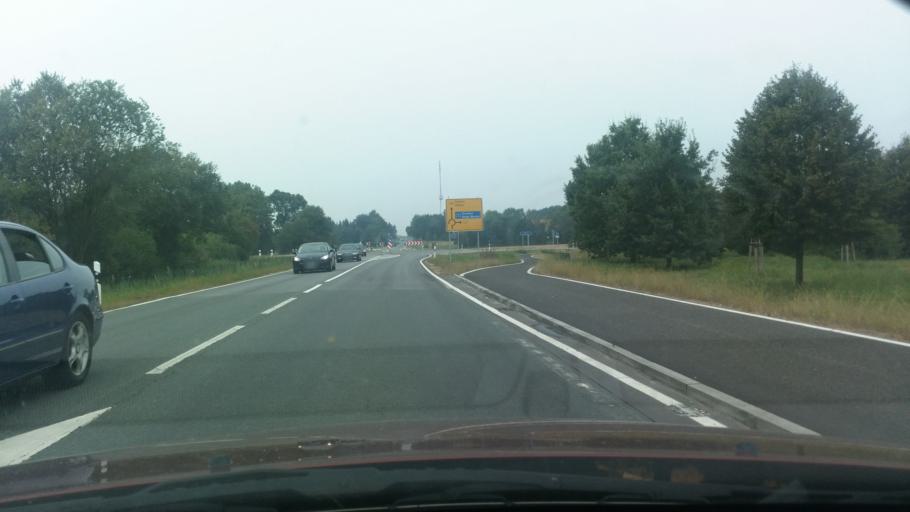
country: DE
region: Saxony
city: Goerlitz
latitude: 51.1910
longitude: 14.9540
